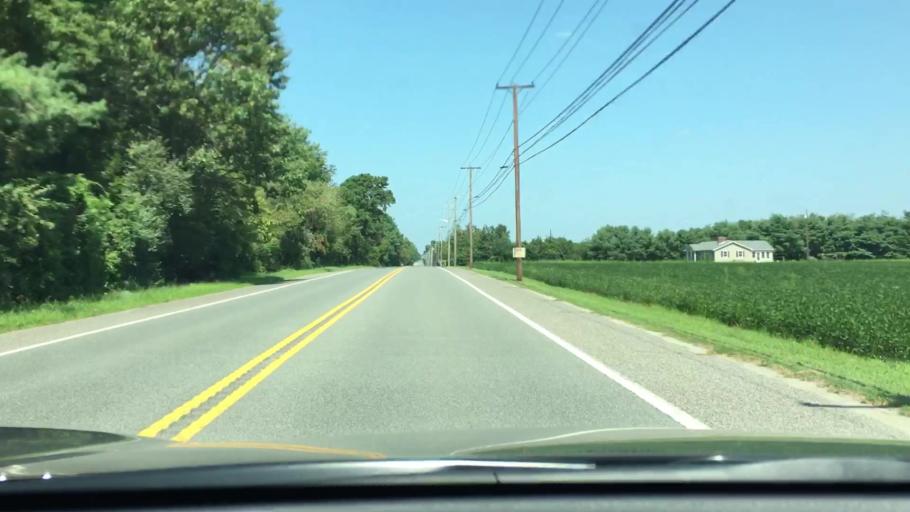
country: US
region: New Jersey
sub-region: Cumberland County
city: Laurel Lake
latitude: 39.2954
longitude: -74.9987
